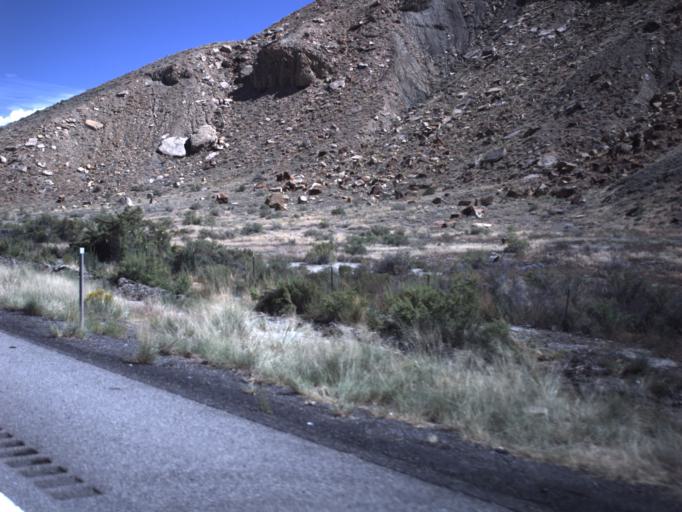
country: US
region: Utah
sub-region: Emery County
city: Ferron
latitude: 38.8088
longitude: -111.2547
